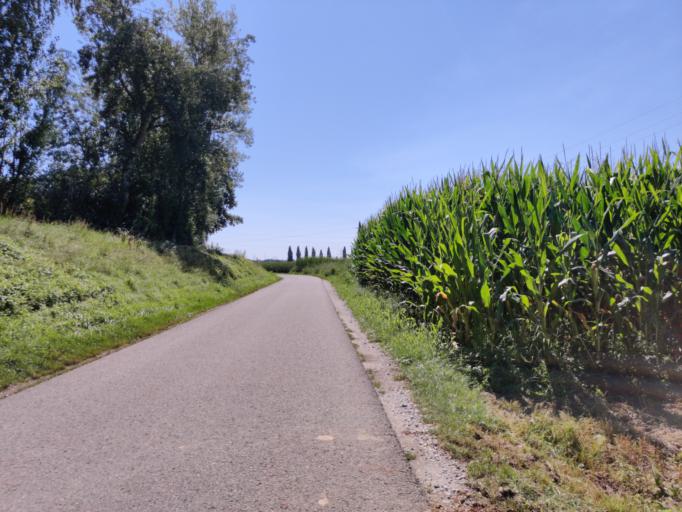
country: AT
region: Styria
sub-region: Politischer Bezirk Leibnitz
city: Ragnitz
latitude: 46.8287
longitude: 15.5623
